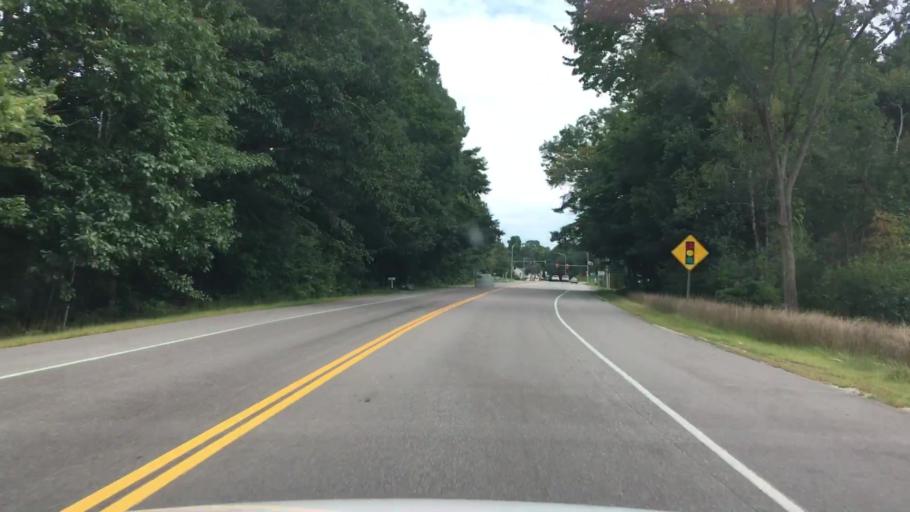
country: US
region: New Hampshire
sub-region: Strafford County
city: Dover
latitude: 43.1850
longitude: -70.8935
